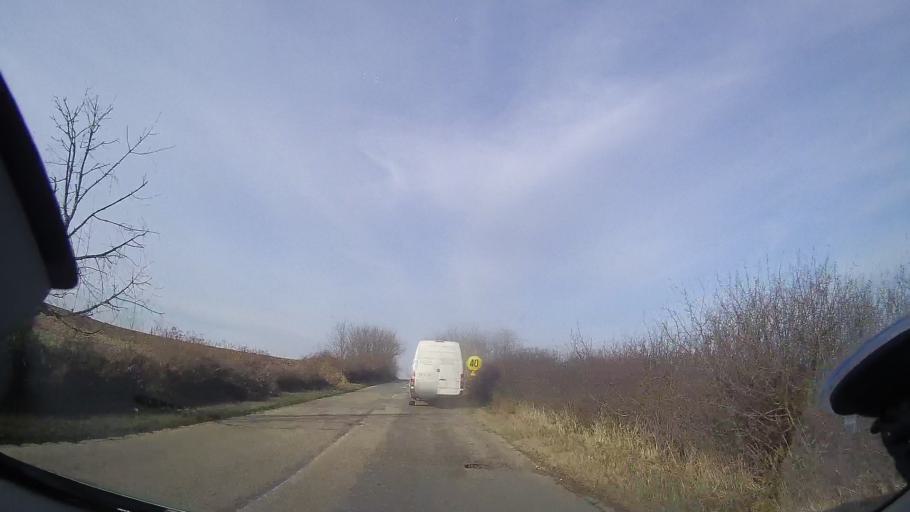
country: RO
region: Bihor
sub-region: Comuna Spinus
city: Spinus
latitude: 47.2078
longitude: 22.1808
